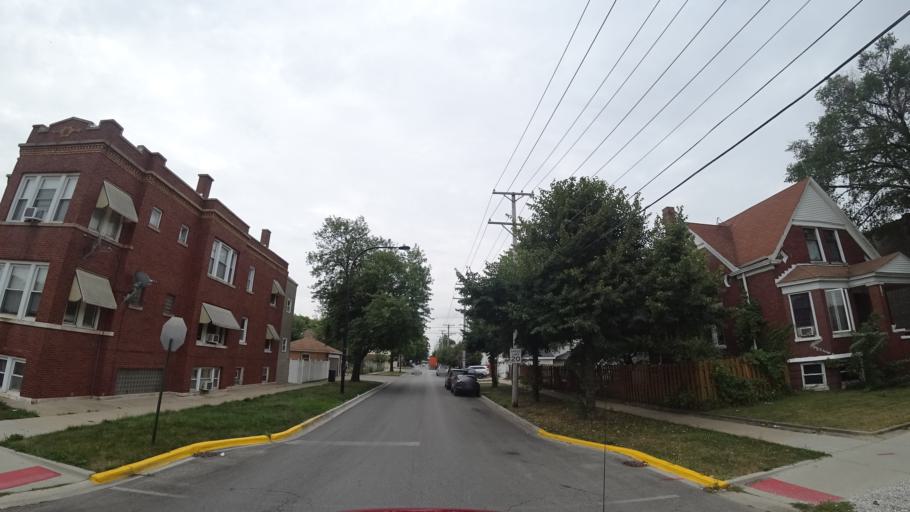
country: US
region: Illinois
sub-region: Cook County
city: Cicero
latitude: 41.8466
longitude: -87.7515
